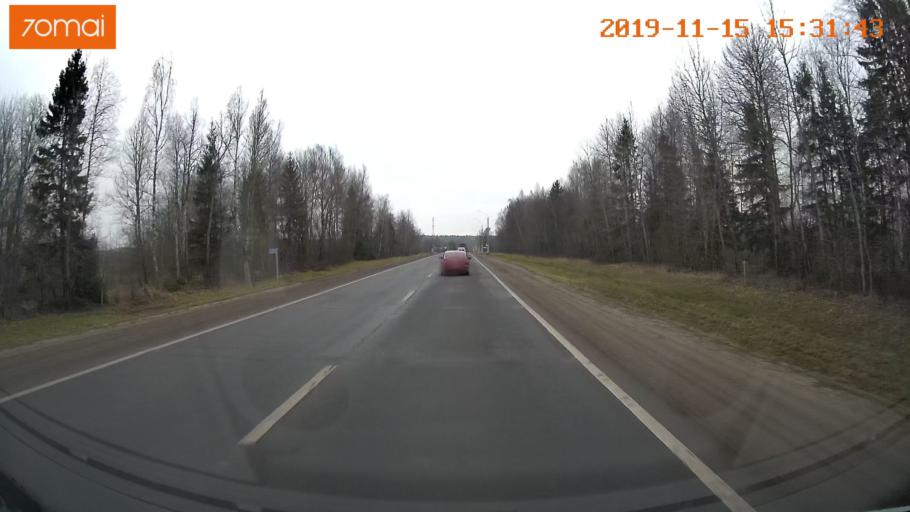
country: RU
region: Jaroslavl
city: Danilov
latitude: 58.0972
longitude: 40.1054
